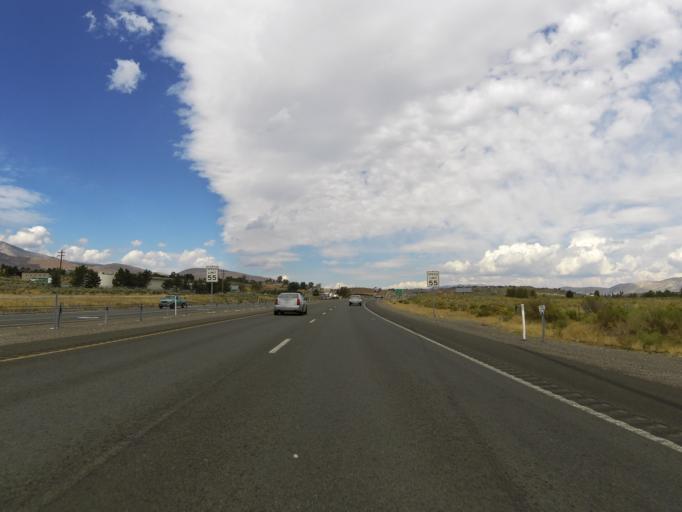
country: US
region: Nevada
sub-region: Douglas County
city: Indian Hills
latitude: 39.0704
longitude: -119.7799
